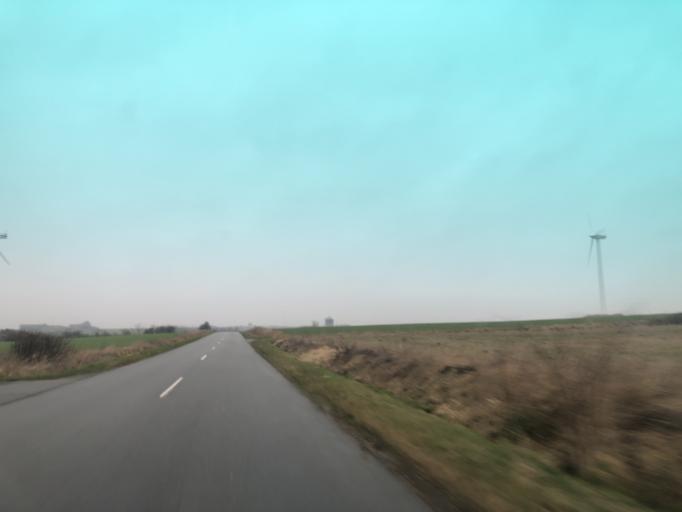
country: DK
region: North Denmark
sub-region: Thisted Kommune
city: Hurup
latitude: 56.7273
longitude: 8.4249
